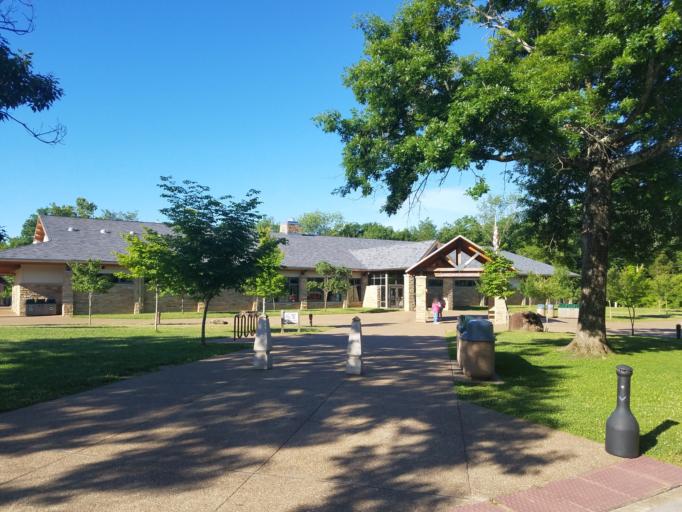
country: US
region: Kentucky
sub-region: Barren County
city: Cave City
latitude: 37.1875
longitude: -86.1009
